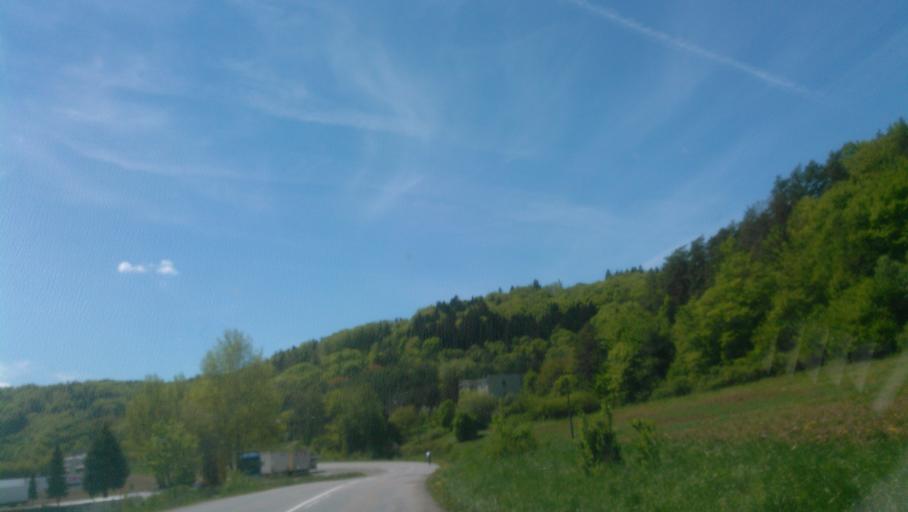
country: SK
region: Banskobystricky
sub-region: Okres Banska Bystrica
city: Banska Bystrica
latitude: 48.7562
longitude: 19.2437
